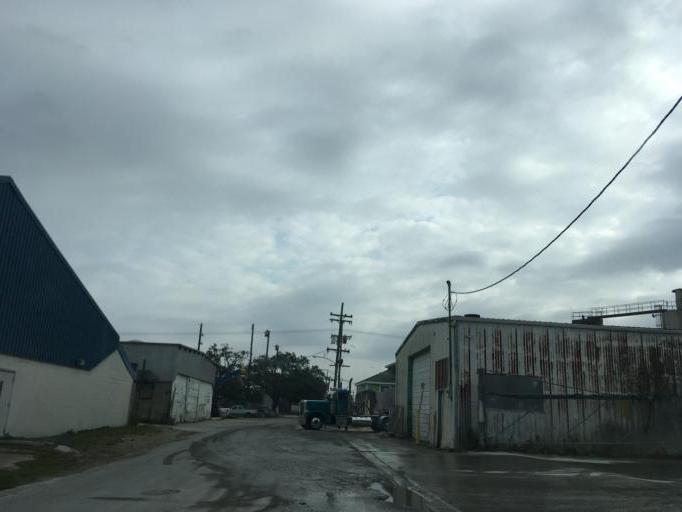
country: US
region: Louisiana
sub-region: Orleans Parish
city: New Orleans
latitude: 29.9875
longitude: -90.0629
